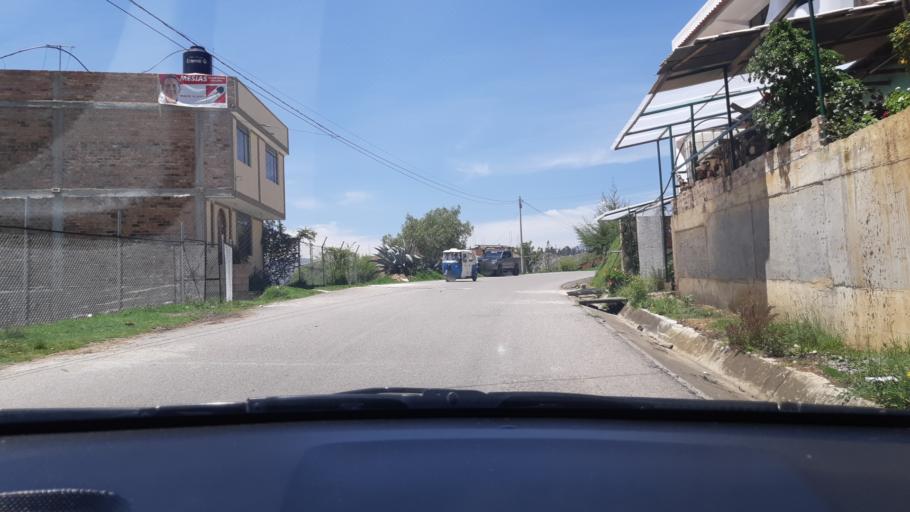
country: PE
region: Cajamarca
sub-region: Provincia de Cajamarca
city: Llacanora
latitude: -7.1794
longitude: -78.4559
